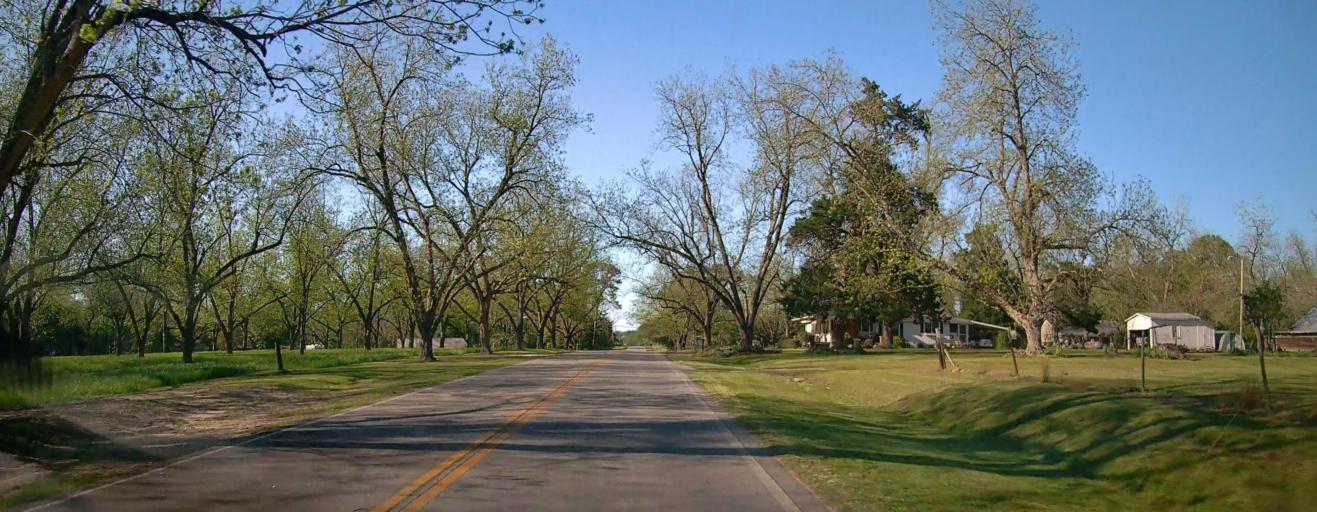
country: US
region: Georgia
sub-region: Ben Hill County
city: Fitzgerald
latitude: 31.7219
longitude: -83.2355
